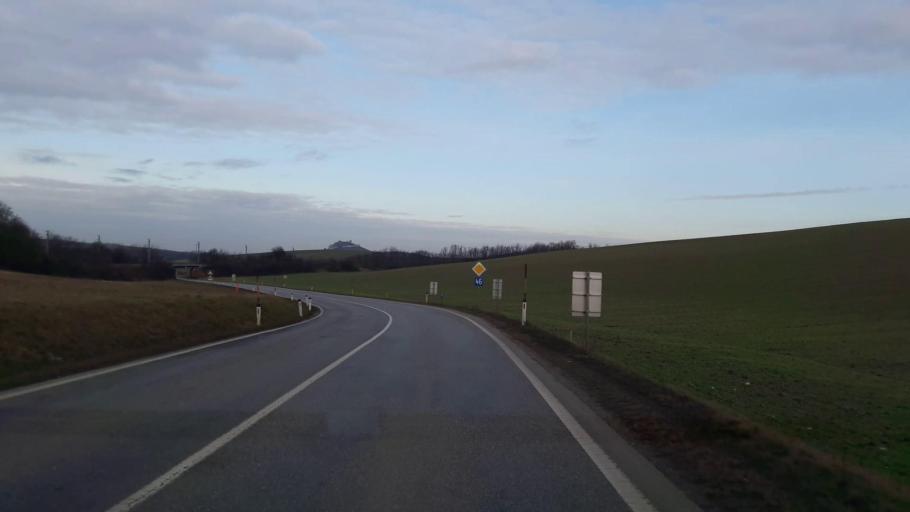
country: AT
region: Lower Austria
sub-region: Politischer Bezirk Mistelbach
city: Staatz
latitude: 48.6485
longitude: 16.5084
